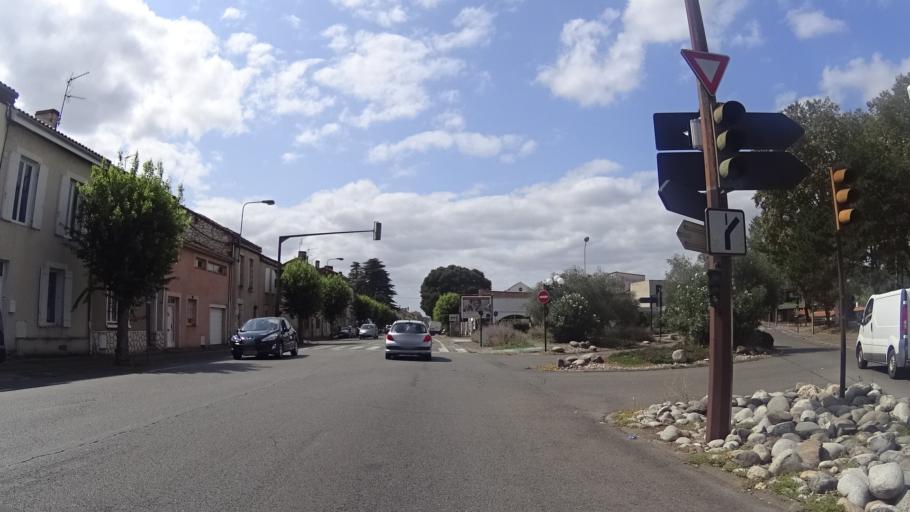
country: FR
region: Aquitaine
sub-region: Departement du Lot-et-Garonne
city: Agen
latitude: 44.2068
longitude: 0.6374
